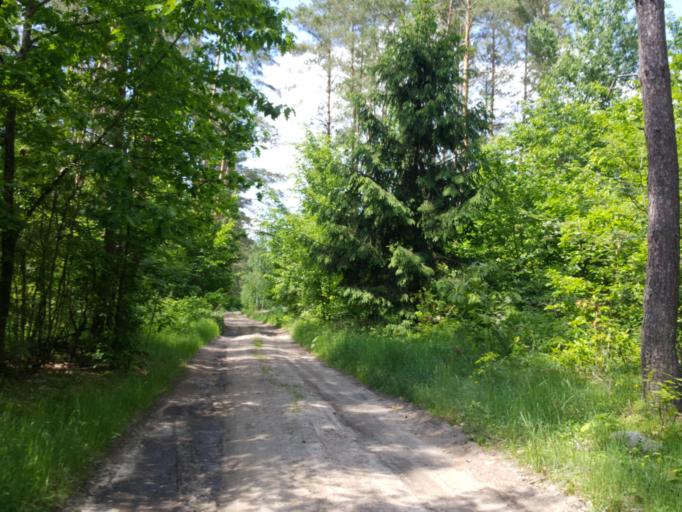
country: PL
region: Podlasie
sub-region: Powiat hajnowski
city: Hajnowka
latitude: 52.5777
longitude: 23.6227
